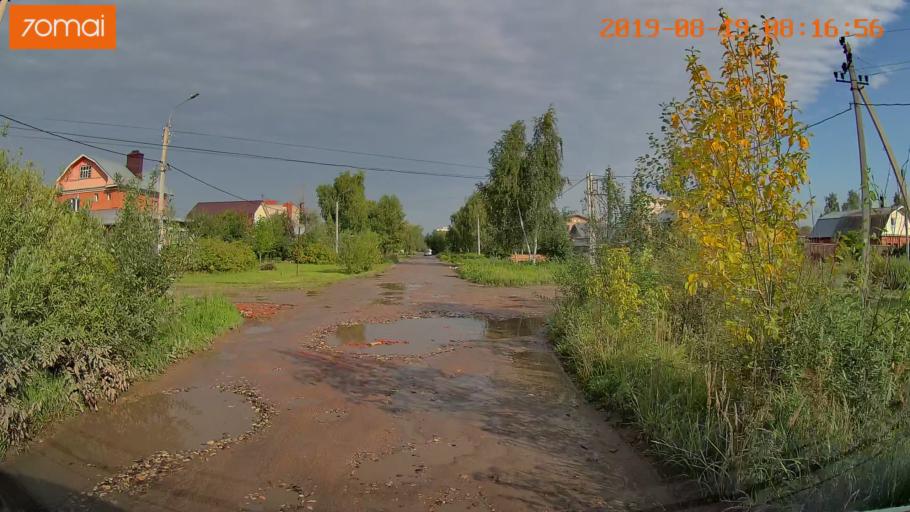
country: RU
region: Ivanovo
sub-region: Gorod Ivanovo
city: Ivanovo
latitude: 56.9754
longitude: 40.9982
